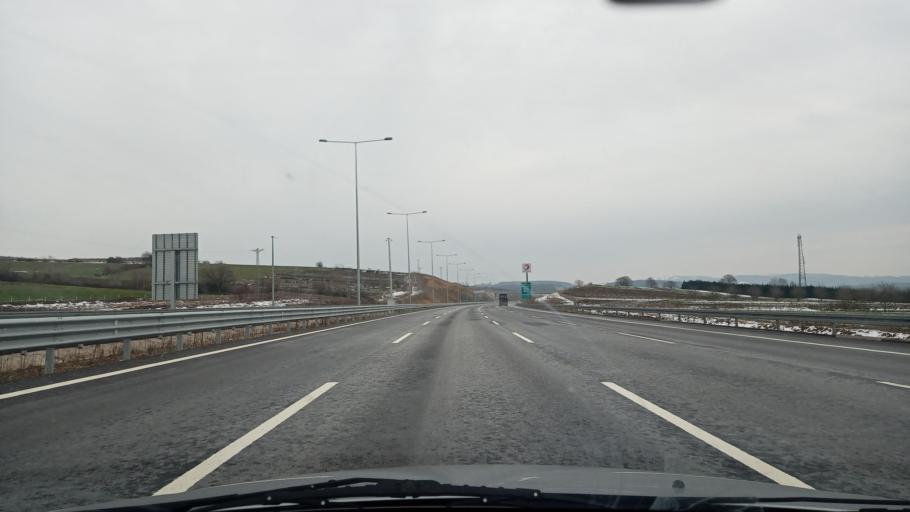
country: TR
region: Kocaeli
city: Derbent
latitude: 40.7966
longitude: 30.0628
